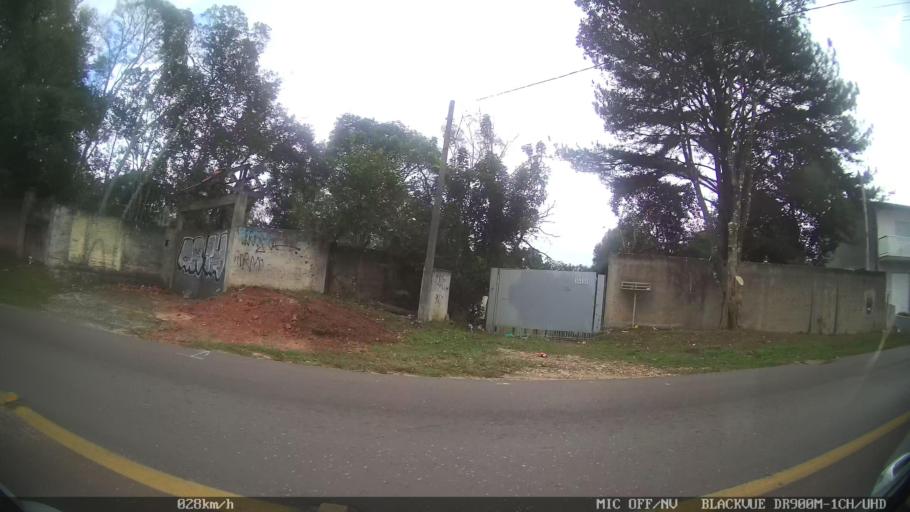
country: BR
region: Parana
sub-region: Almirante Tamandare
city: Almirante Tamandare
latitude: -25.3609
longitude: -49.2516
